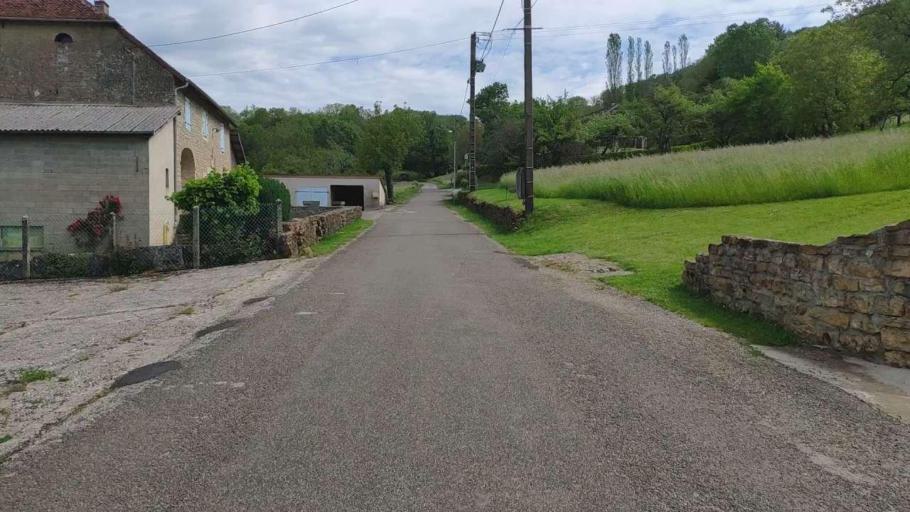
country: FR
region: Franche-Comte
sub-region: Departement du Jura
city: Poligny
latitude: 46.7708
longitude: 5.6238
